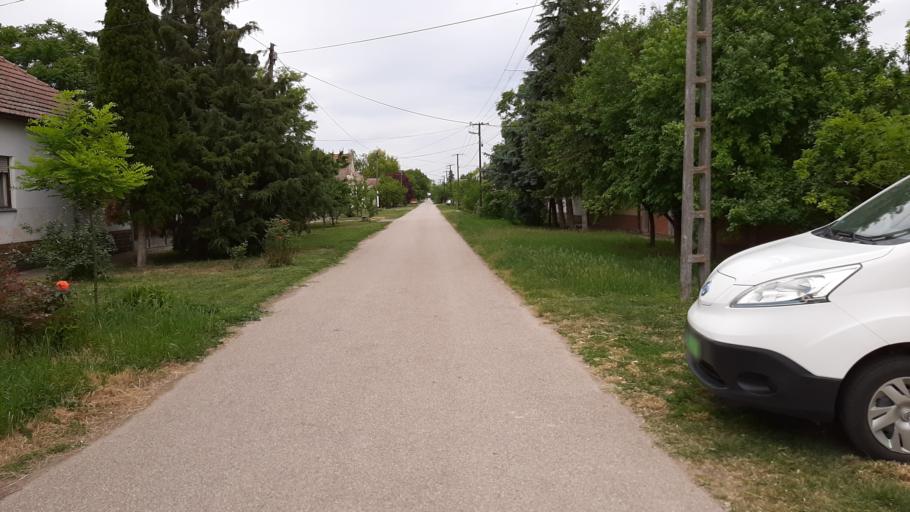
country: RO
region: Timis
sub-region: Comuna Beba Veche
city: Beba Veche
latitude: 46.1456
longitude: 20.2775
